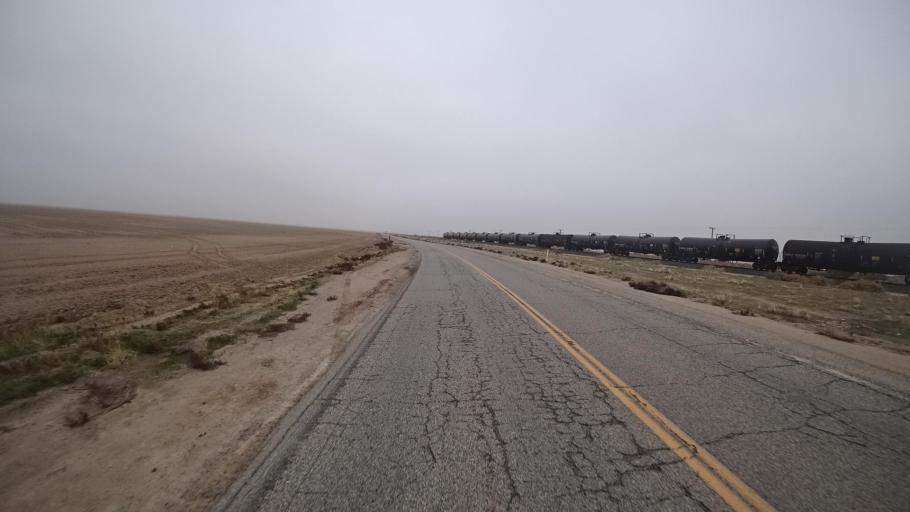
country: US
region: California
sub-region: Kern County
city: Maricopa
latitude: 35.1234
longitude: -119.2655
